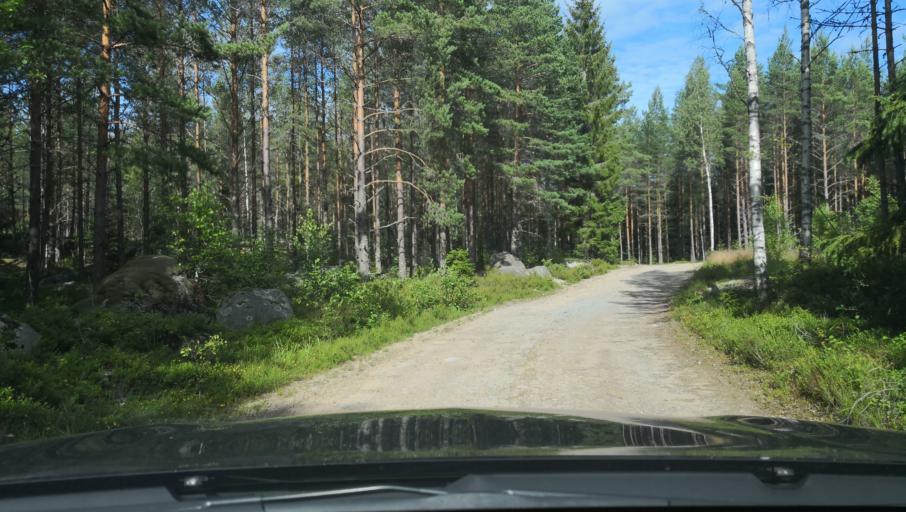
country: SE
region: Vaestmanland
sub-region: Surahammars Kommun
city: Surahammar
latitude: 59.6729
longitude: 16.1090
